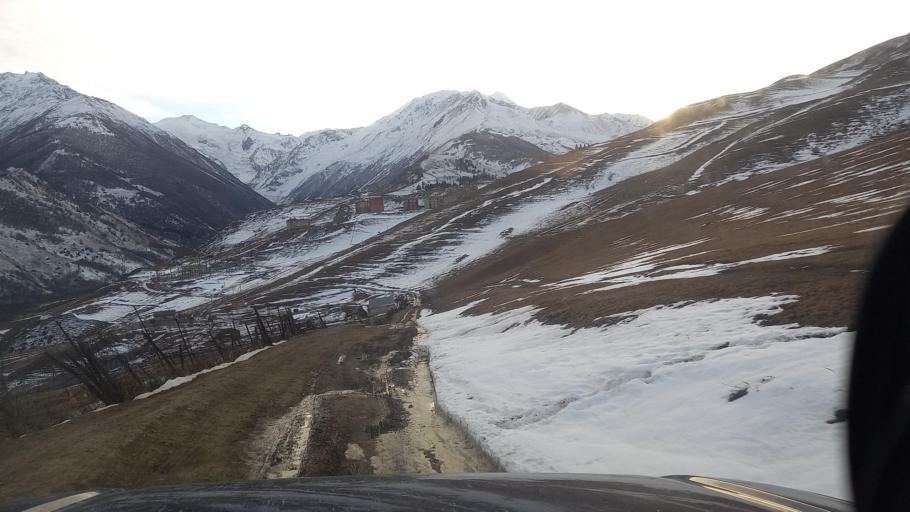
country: RU
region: Ingushetiya
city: Dzhayrakh
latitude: 42.8520
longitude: 44.5146
